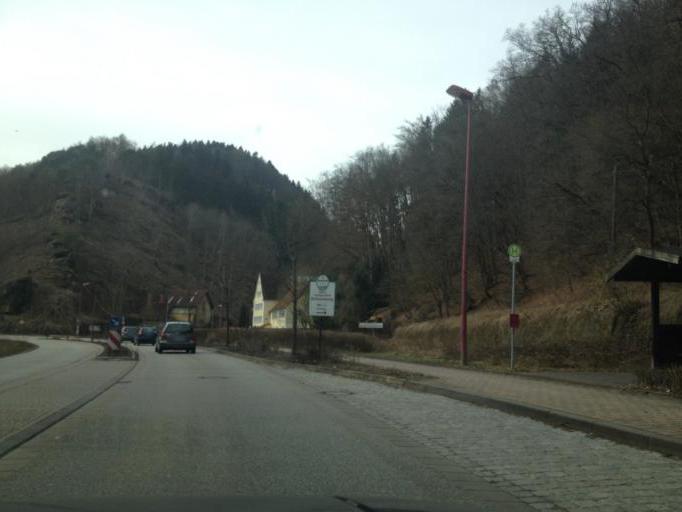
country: DE
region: Rheinland-Pfalz
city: Frankenstein
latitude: 49.4396
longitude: 7.9686
